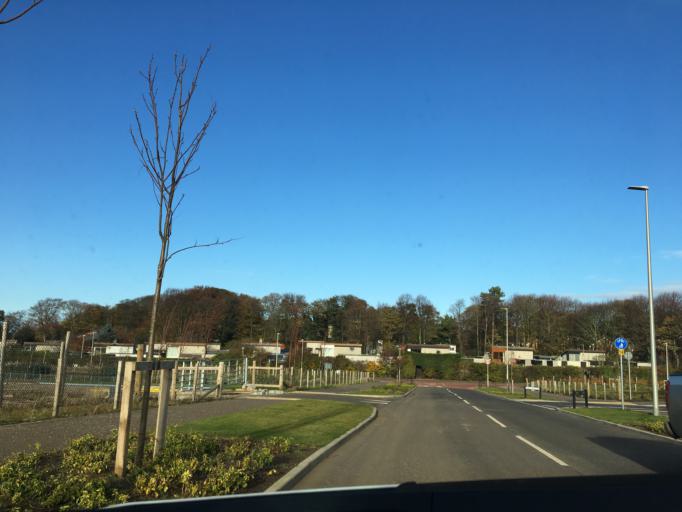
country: GB
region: Scotland
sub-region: East Lothian
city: North Berwick
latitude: 56.0508
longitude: -2.7282
